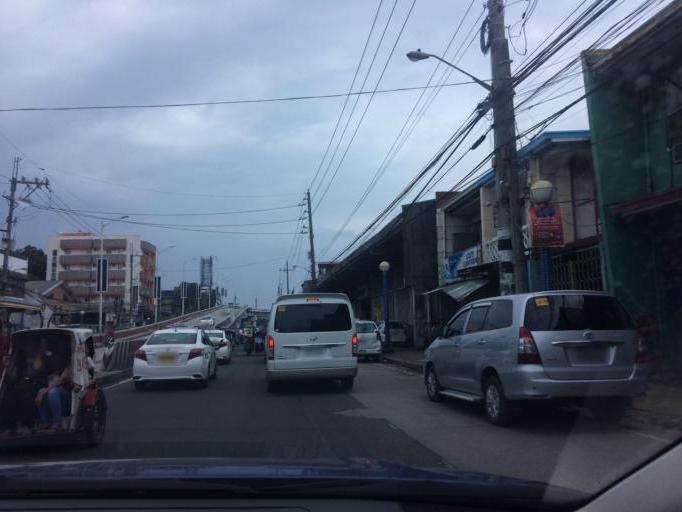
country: PH
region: Metro Manila
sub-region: Makati City
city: Makati City
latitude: 14.5350
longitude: 121.0035
